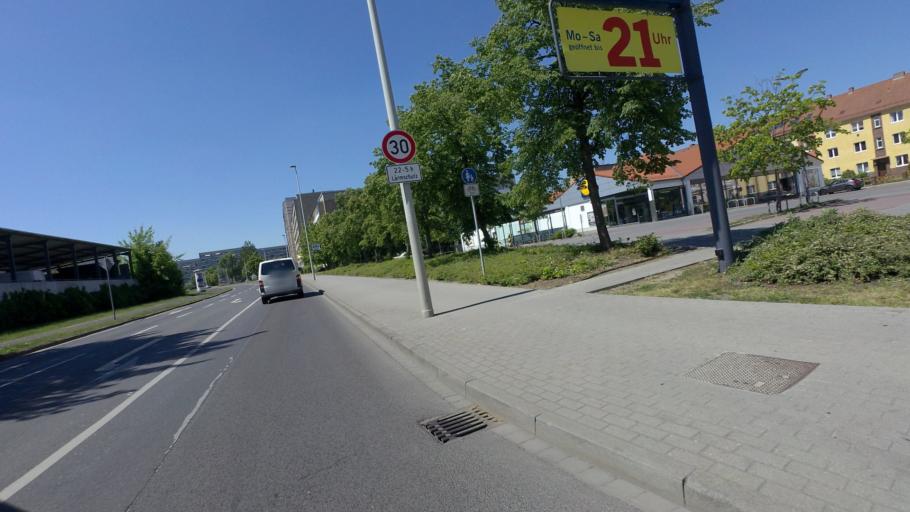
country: DE
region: Brandenburg
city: Cottbus
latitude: 51.7624
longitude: 14.3530
